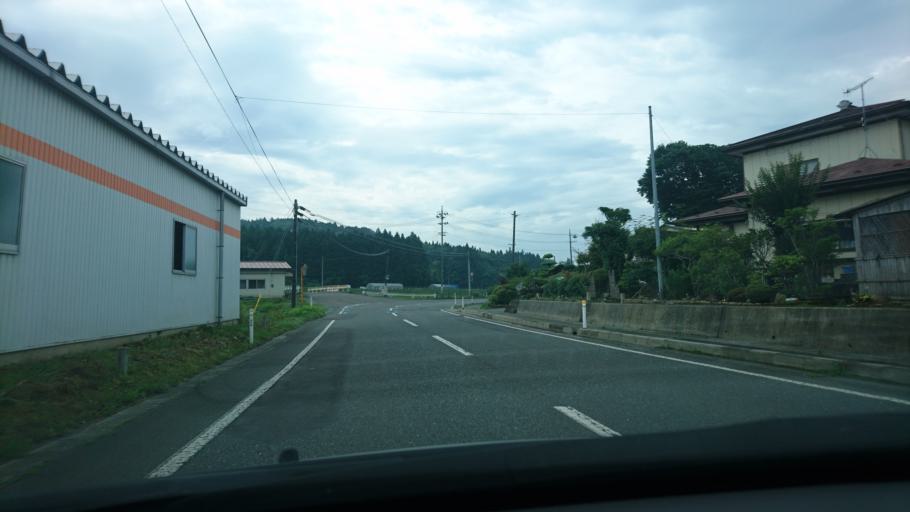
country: JP
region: Iwate
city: Ichinoseki
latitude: 38.9334
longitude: 141.4265
